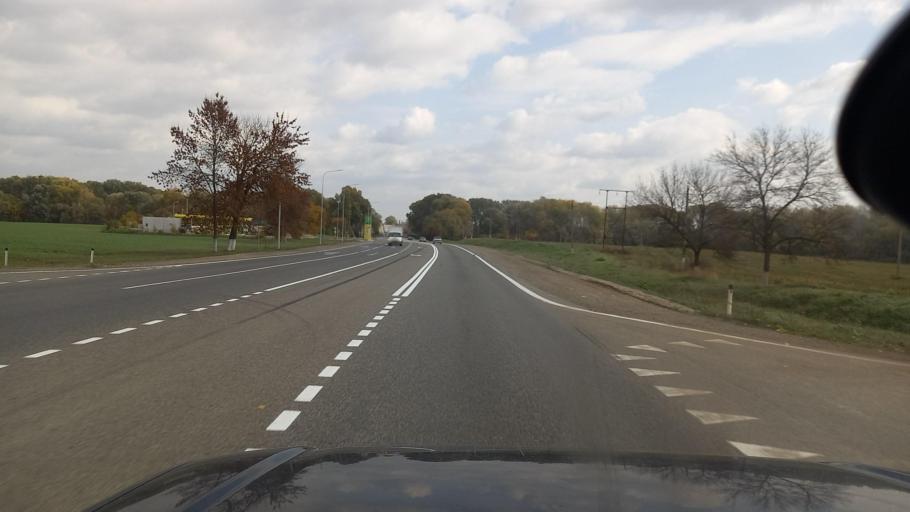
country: RU
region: Krasnodarskiy
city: Chernomorskiy
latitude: 44.8523
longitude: 38.4464
